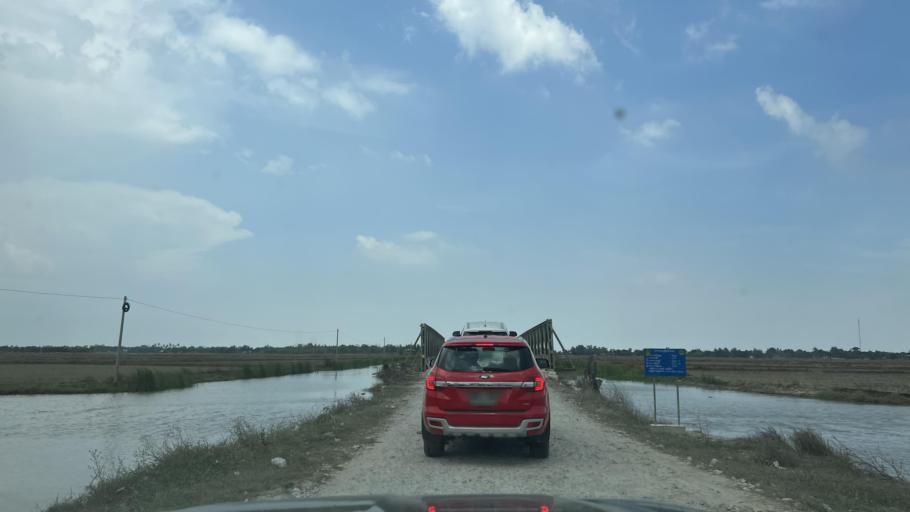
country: MM
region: Ayeyarwady
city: Pyapon
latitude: 16.0761
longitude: 95.6207
